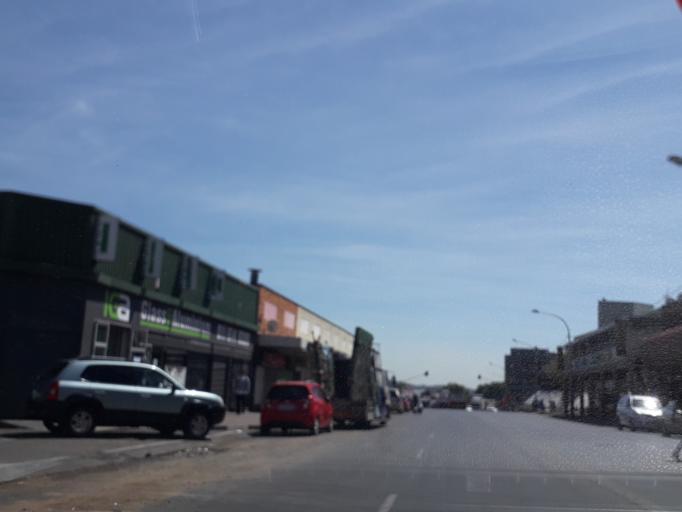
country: ZA
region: Gauteng
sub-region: City of Johannesburg Metropolitan Municipality
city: Johannesburg
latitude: -26.1987
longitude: 28.0666
